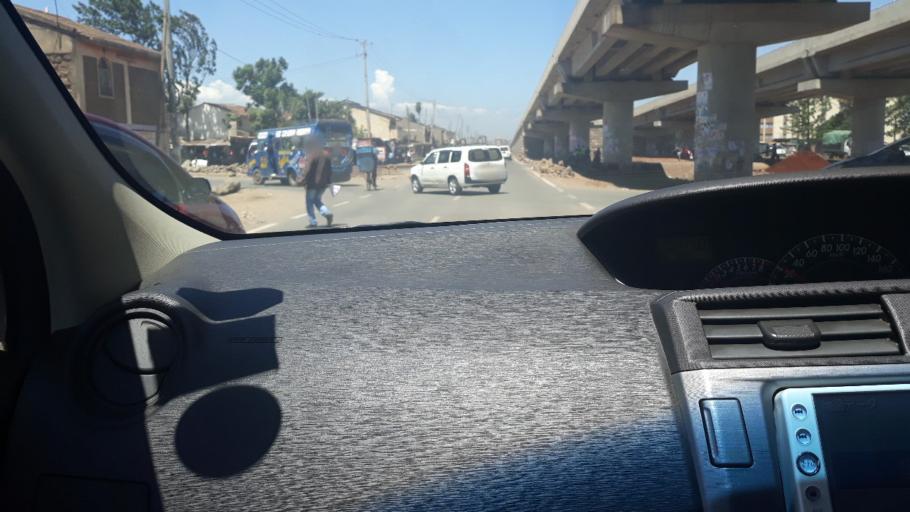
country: KE
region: Nairobi Area
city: Pumwani
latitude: -1.2720
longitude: 36.8811
